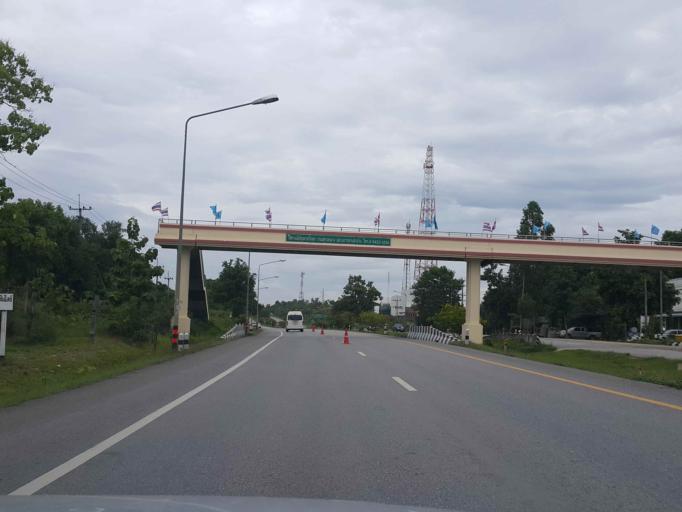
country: TH
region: Lampang
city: Thoen
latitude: 17.6145
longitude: 99.2304
